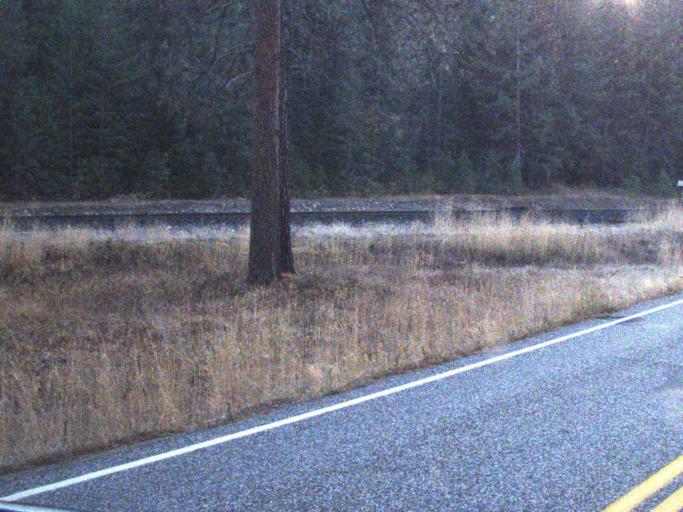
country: US
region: Washington
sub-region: Stevens County
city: Kettle Falls
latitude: 48.8153
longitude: -117.9755
